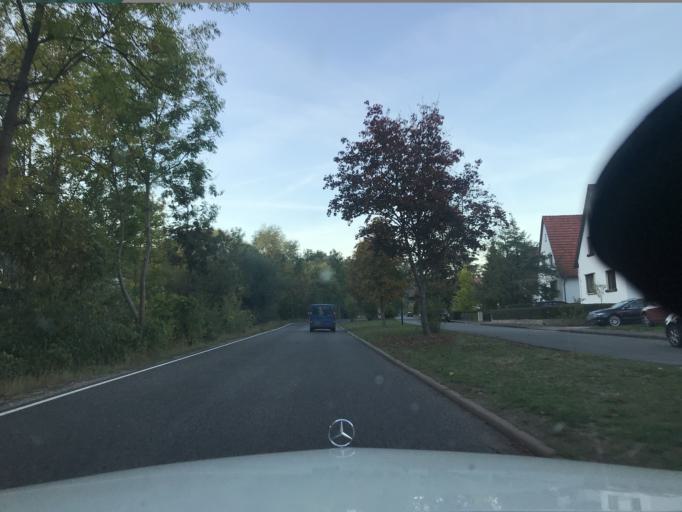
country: DE
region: Hesse
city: Wanfried
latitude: 51.1964
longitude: 10.1271
